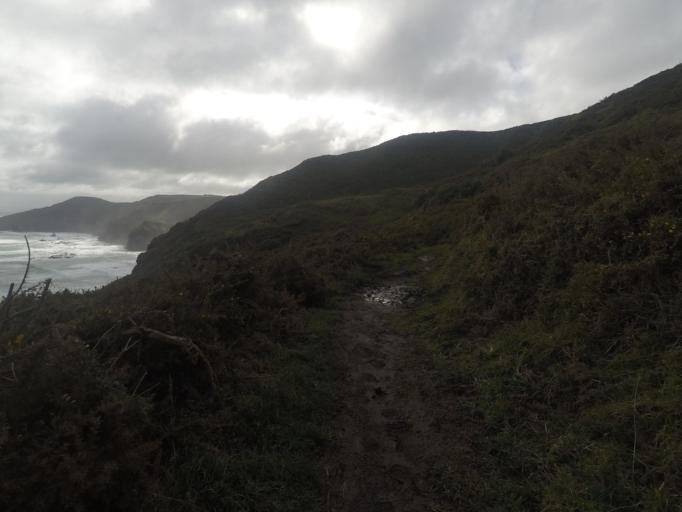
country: NZ
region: Auckland
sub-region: Auckland
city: Muriwai Beach
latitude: -36.8740
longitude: 174.4324
